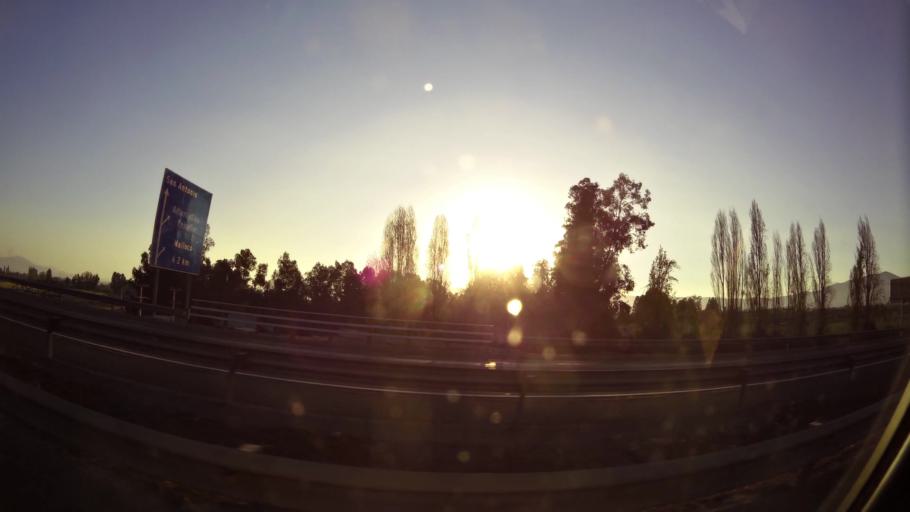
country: CL
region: Santiago Metropolitan
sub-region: Provincia de Talagante
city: Penaflor
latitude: -33.5892
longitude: -70.8449
